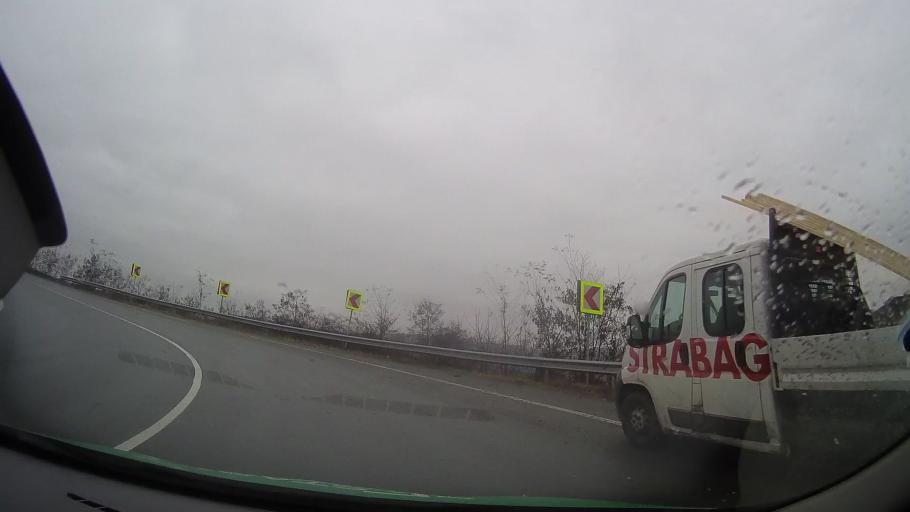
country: RO
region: Bistrita-Nasaud
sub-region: Comuna Teaca
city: Teaca
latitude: 46.9031
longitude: 24.4987
